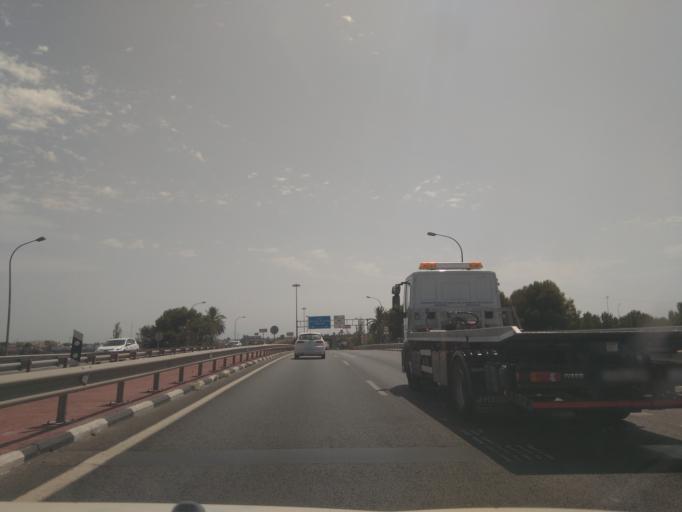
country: ES
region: Valencia
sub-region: Provincia de Valencia
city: Sedavi
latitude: 39.4354
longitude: -0.3703
